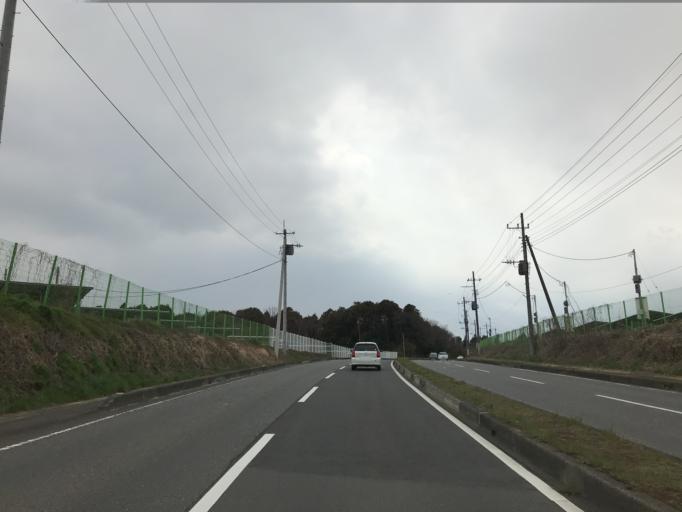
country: JP
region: Ibaraki
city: Ushiku
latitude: 35.9978
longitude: 140.0742
